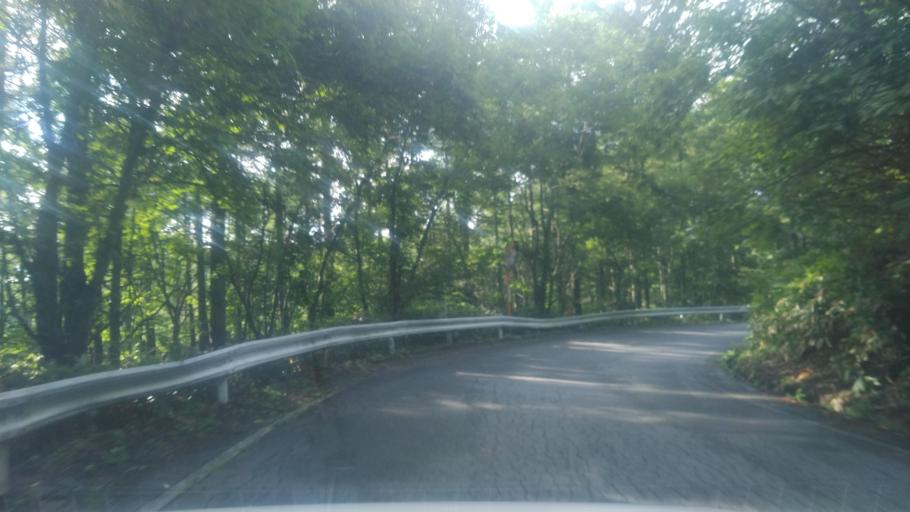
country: JP
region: Nagano
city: Ueda
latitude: 36.5064
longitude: 138.3749
